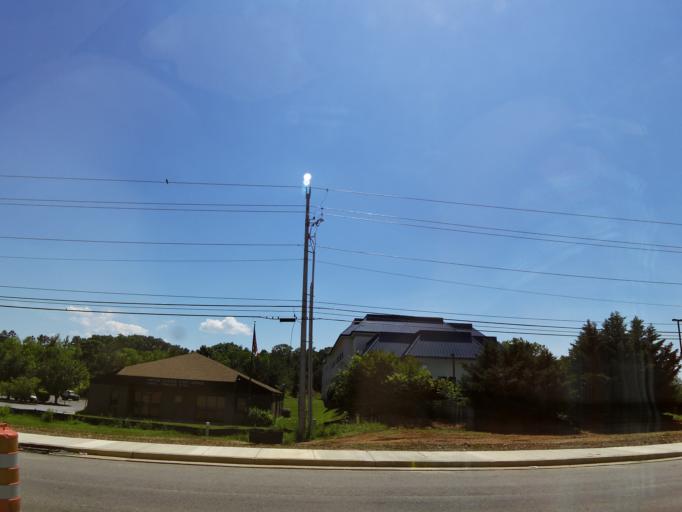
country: US
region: Tennessee
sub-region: Sevier County
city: Sevierville
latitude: 35.9532
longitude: -83.5904
